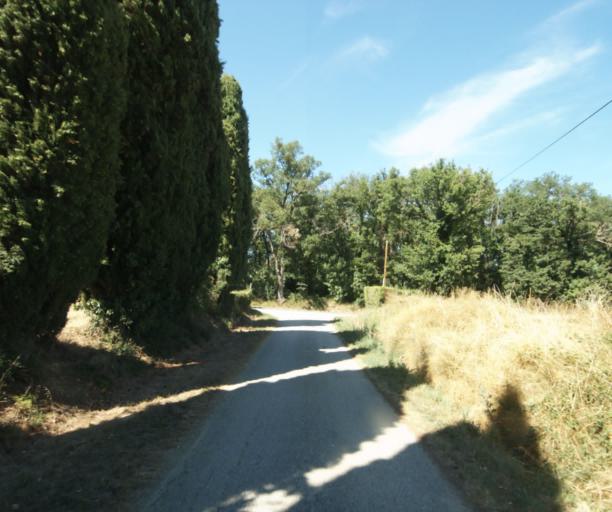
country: FR
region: Midi-Pyrenees
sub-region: Departement de la Haute-Garonne
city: Saint-Felix-Lauragais
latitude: 43.5106
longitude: 1.9147
